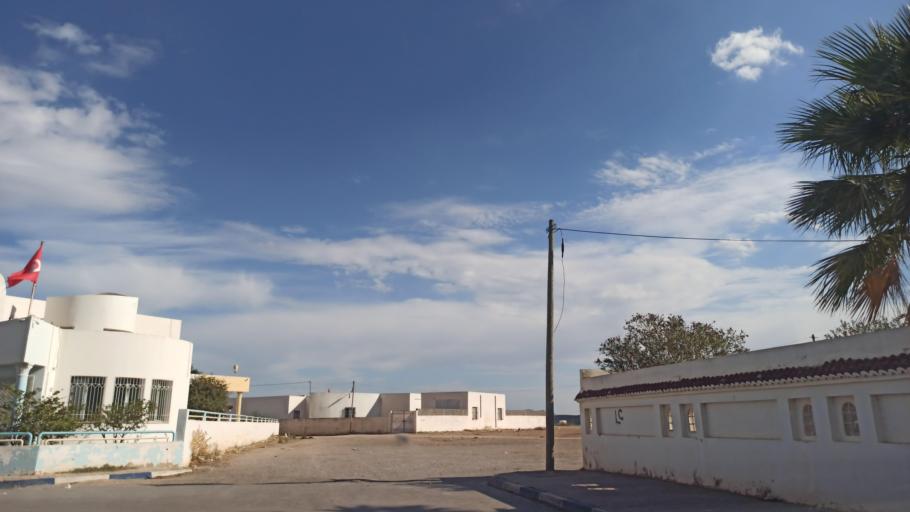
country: TN
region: Zaghwan
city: Zaghouan
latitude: 36.3548
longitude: 10.2117
